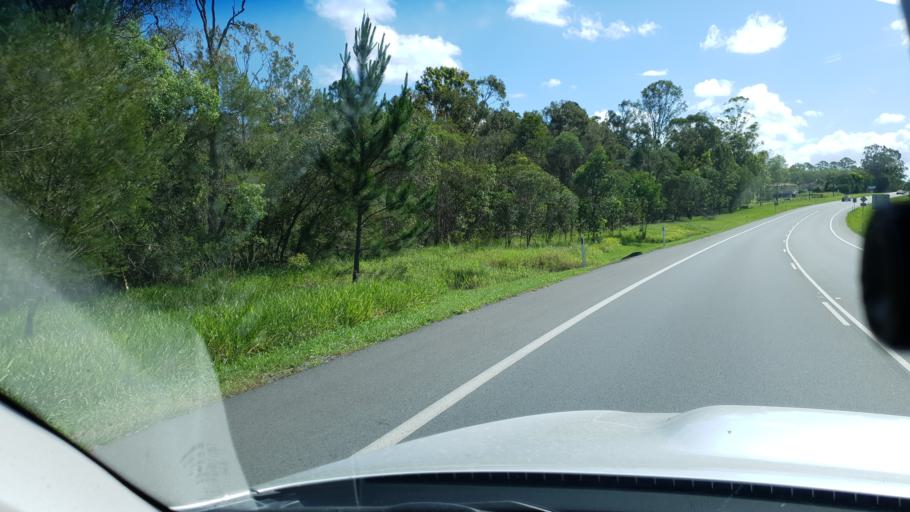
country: AU
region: Queensland
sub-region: Logan
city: Woodridge
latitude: -27.6492
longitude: 153.0851
